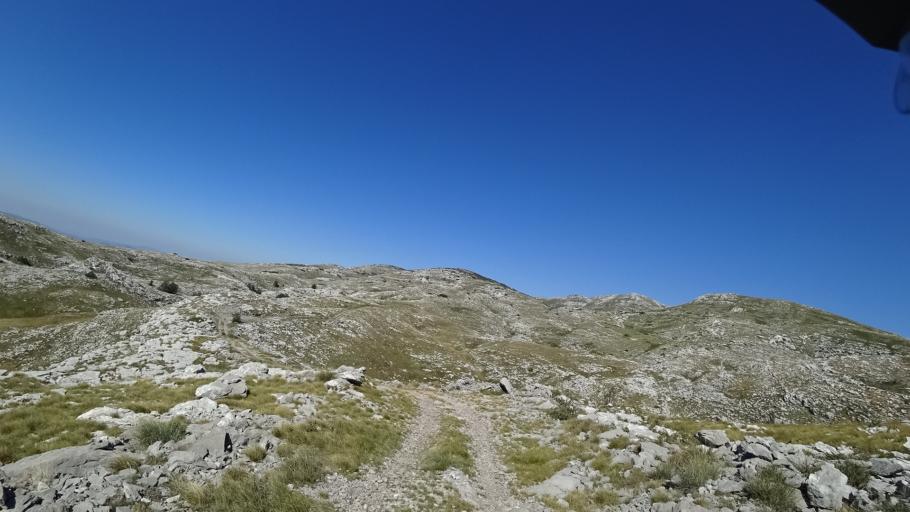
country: HR
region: Splitsko-Dalmatinska
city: Hrvace
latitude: 43.9256
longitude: 16.6060
